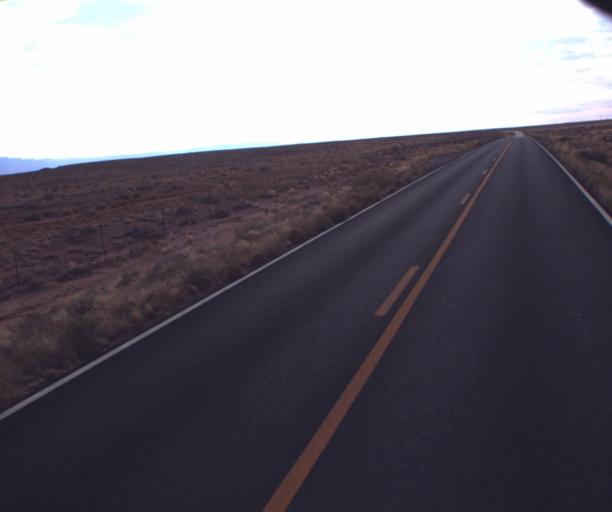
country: US
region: Arizona
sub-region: Apache County
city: Many Farms
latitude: 36.5695
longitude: -109.5467
